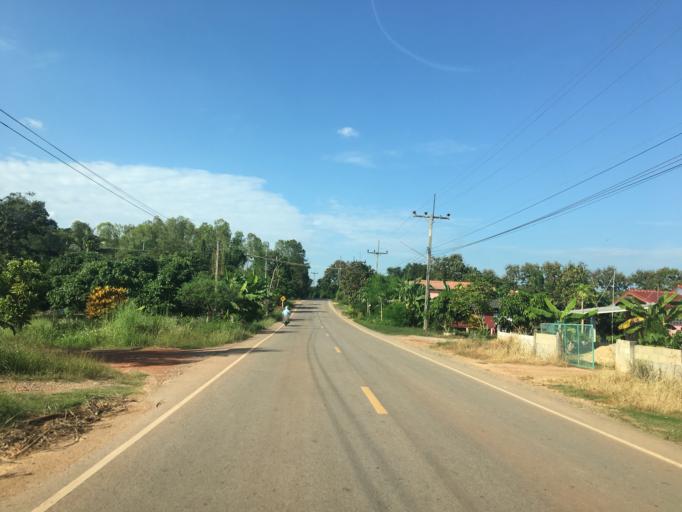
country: TH
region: Chiang Rai
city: Pa Daet
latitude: 19.4272
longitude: 100.0145
